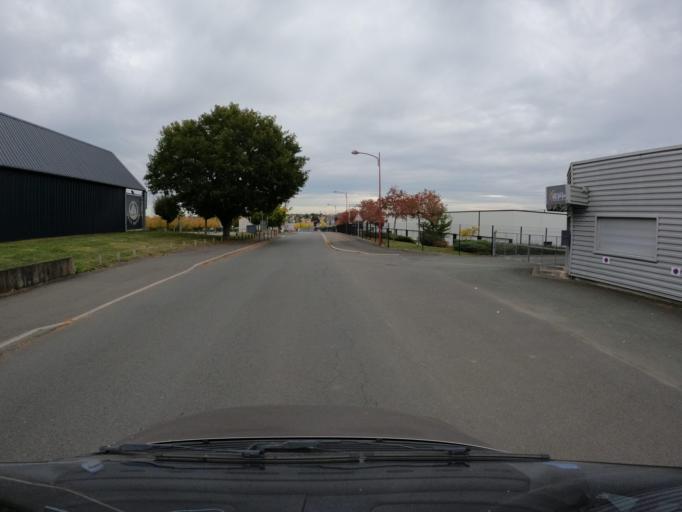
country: FR
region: Pays de la Loire
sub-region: Departement de Maine-et-Loire
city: La Seguiniere
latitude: 47.0548
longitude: -0.9400
